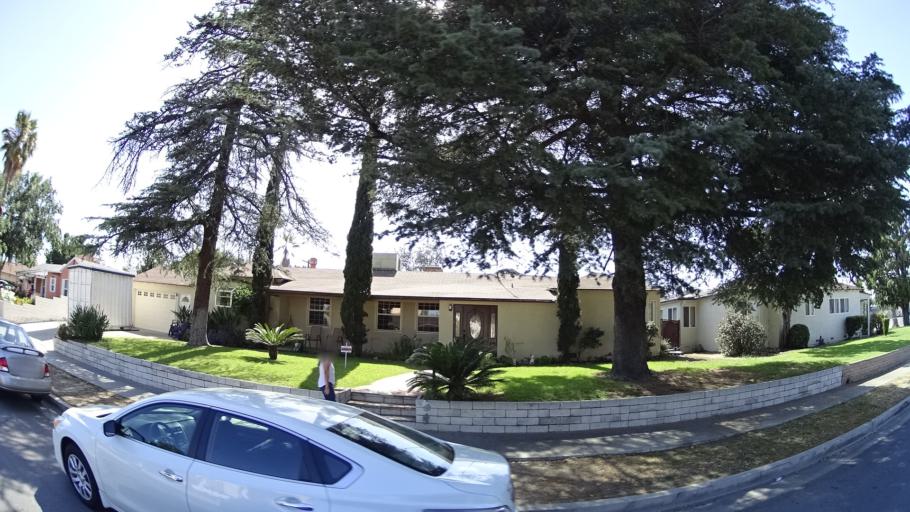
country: US
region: California
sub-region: Los Angeles County
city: North Hollywood
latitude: 34.1773
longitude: -118.3682
